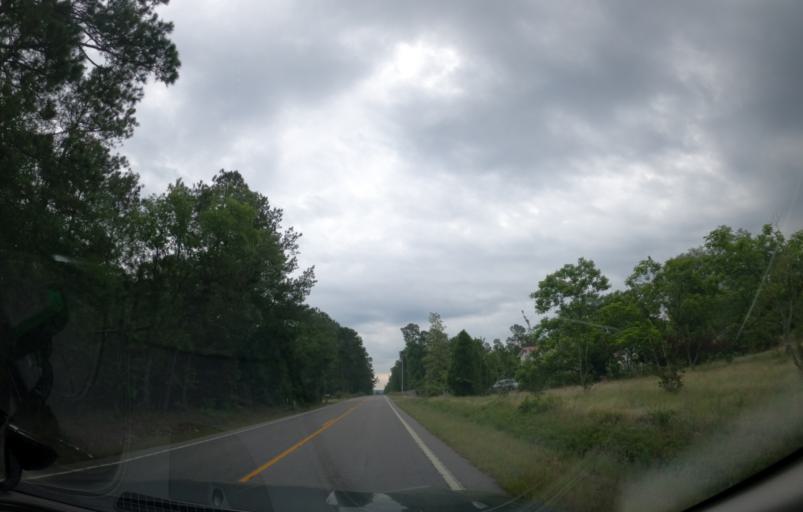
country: US
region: South Carolina
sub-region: Aiken County
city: Aiken
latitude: 33.5740
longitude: -81.6369
